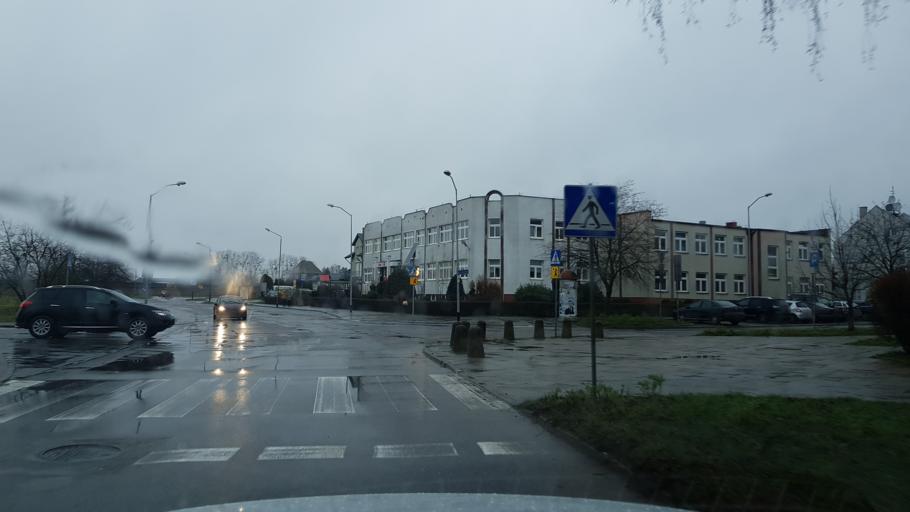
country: PL
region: West Pomeranian Voivodeship
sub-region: Powiat stargardzki
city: Stargard Szczecinski
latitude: 53.3157
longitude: 15.0337
